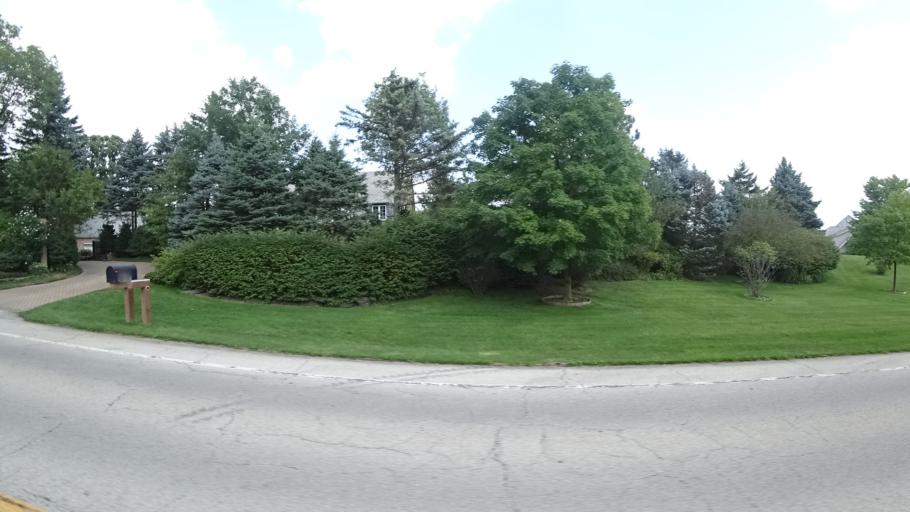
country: US
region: Illinois
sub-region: Will County
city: Goodings Grove
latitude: 41.6576
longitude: -87.8930
